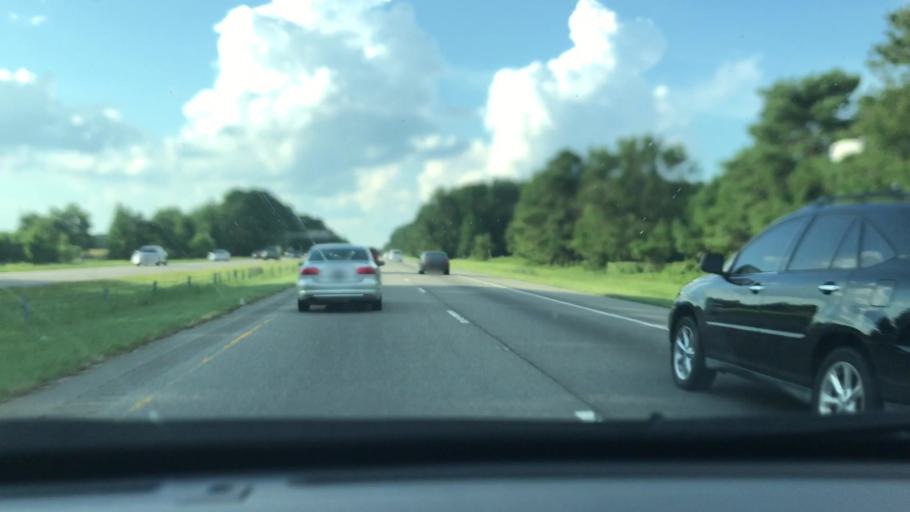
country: US
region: North Carolina
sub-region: Robeson County
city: Saint Pauls
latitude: 34.7462
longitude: -78.9970
